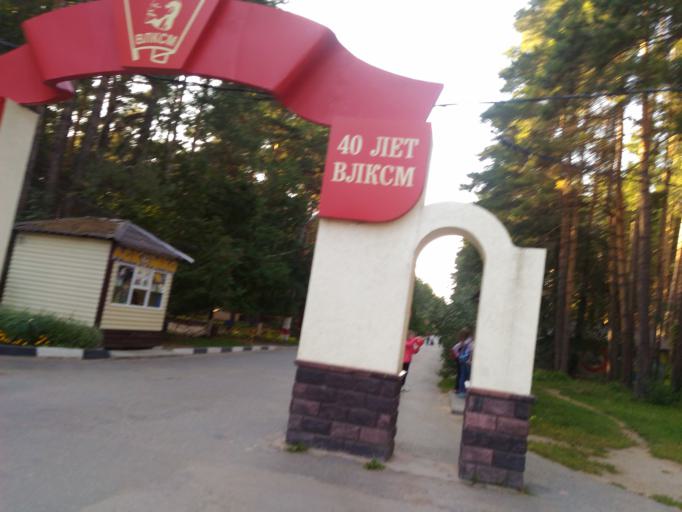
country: RU
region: Ulyanovsk
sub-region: Ulyanovskiy Rayon
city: Ulyanovsk
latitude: 54.3535
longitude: 48.5247
